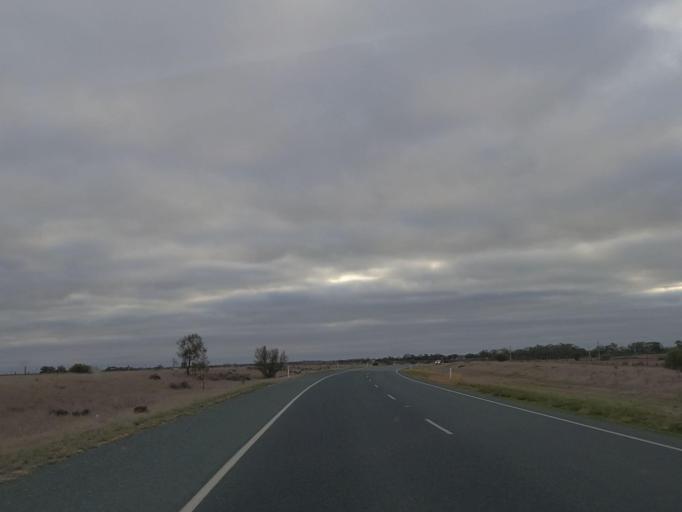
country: AU
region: Victoria
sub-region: Swan Hill
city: Swan Hill
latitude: -35.6258
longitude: 143.8077
